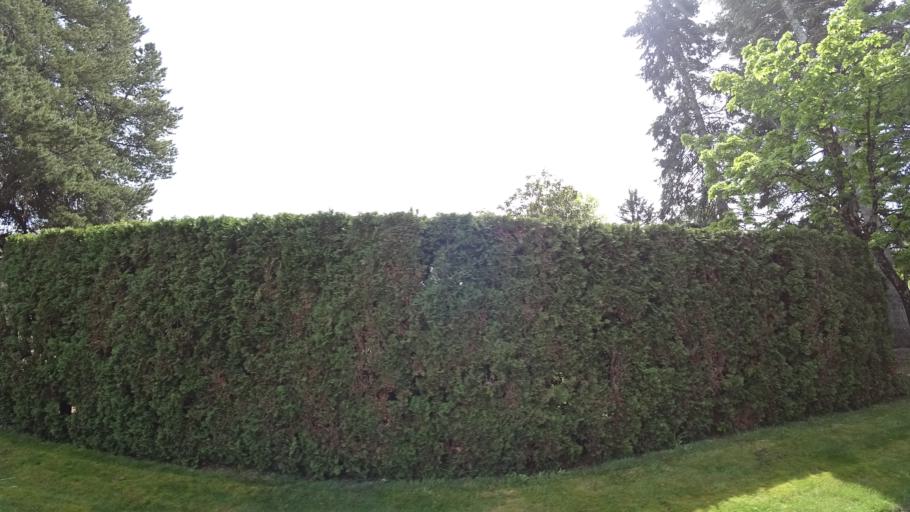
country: US
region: Oregon
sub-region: Washington County
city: Aloha
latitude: 45.4824
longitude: -122.8874
